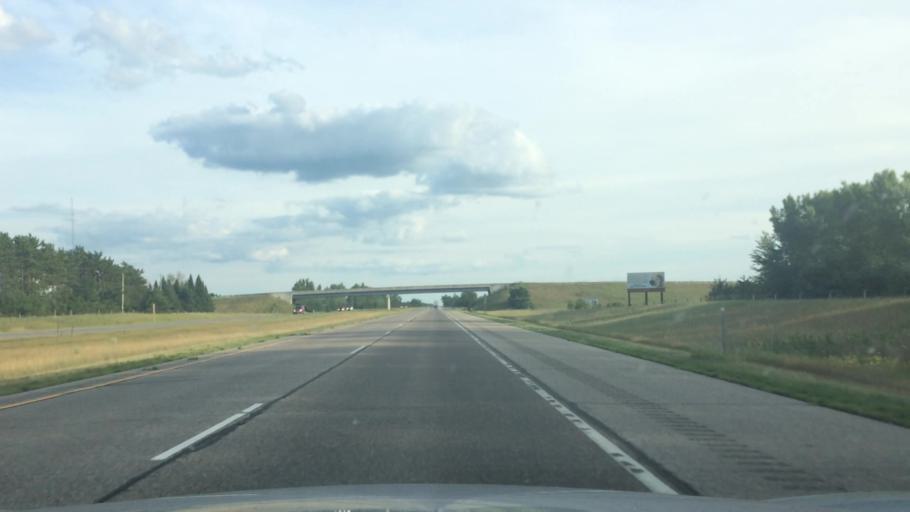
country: US
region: Wisconsin
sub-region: Portage County
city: Plover
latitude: 44.2904
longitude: -89.5237
